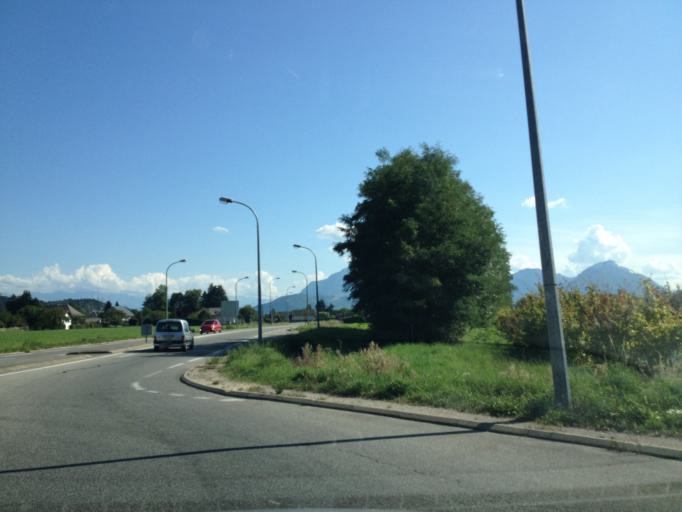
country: FR
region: Rhone-Alpes
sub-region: Departement de la Savoie
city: Sonnaz
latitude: 45.6096
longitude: 5.9104
